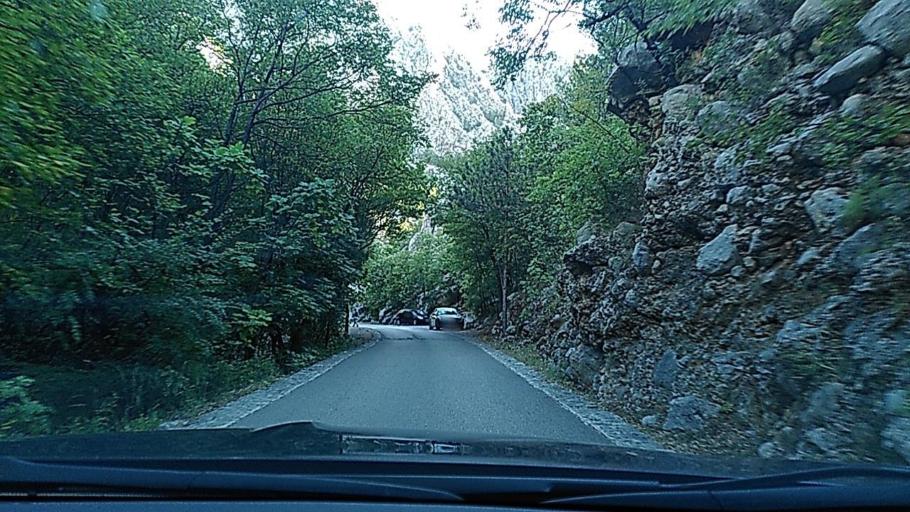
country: HR
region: Zadarska
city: Starigrad
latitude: 44.3006
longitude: 15.4702
